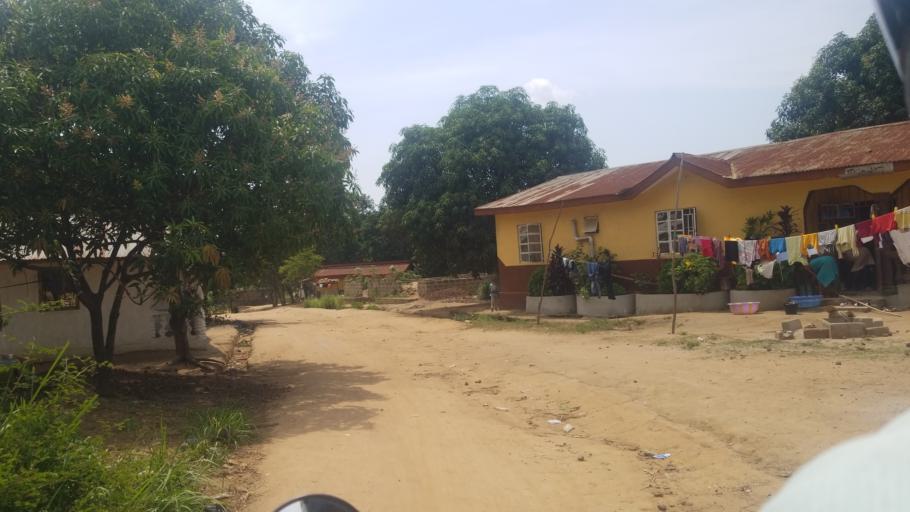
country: SL
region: Western Area
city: Waterloo
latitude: 8.3158
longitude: -13.0477
